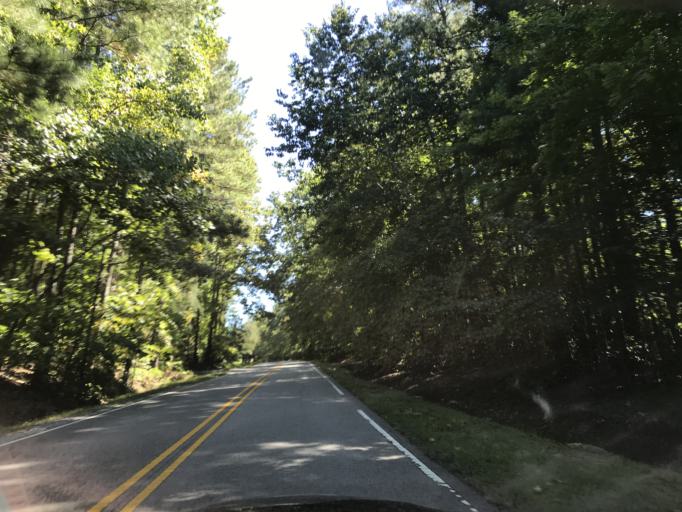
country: US
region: North Carolina
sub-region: Wake County
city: Wake Forest
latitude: 35.9497
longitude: -78.6069
